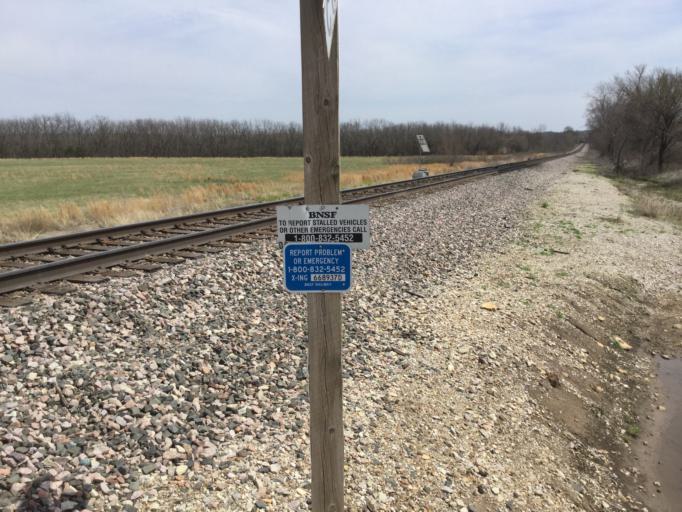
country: US
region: Kansas
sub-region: Bourbon County
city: Fort Scott
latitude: 37.7708
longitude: -94.6678
